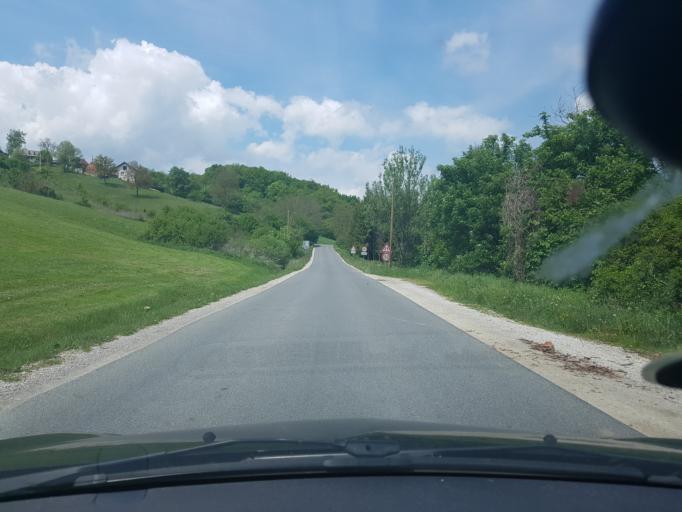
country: HR
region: Krapinsko-Zagorska
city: Pregrada
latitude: 46.1891
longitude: 15.7242
